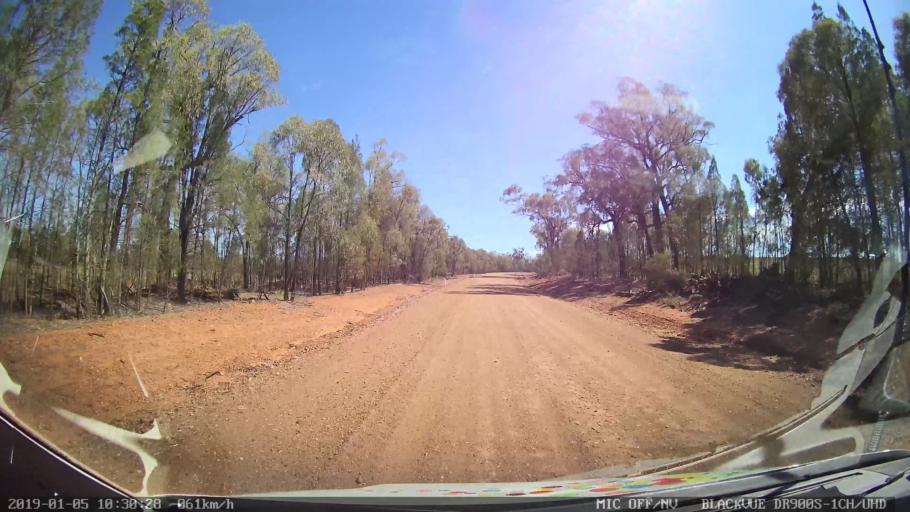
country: AU
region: New South Wales
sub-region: Gilgandra
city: Gilgandra
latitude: -31.5321
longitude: 148.9247
